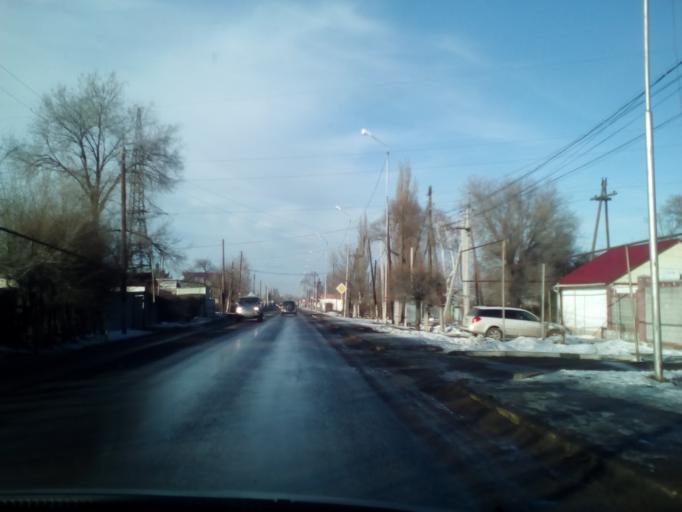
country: KZ
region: Almaty Oblysy
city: Burunday
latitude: 43.1685
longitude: 76.4164
